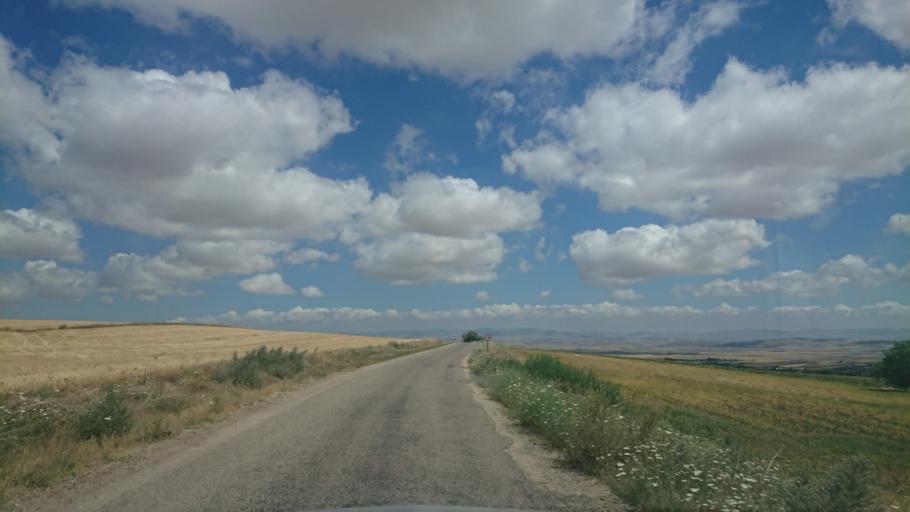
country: TR
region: Aksaray
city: Agacoren
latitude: 38.8459
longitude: 33.9492
